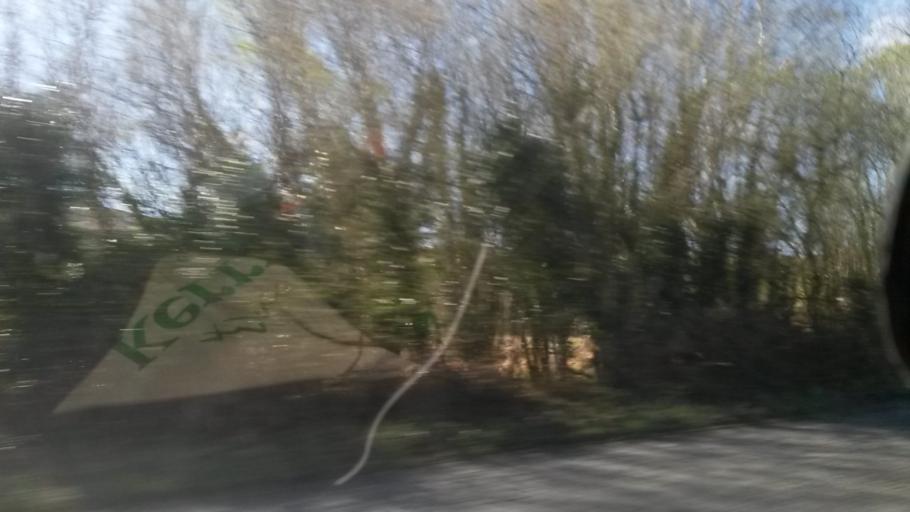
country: IE
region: Munster
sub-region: Ciarrai
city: Cill Airne
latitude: 51.9150
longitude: -9.3947
